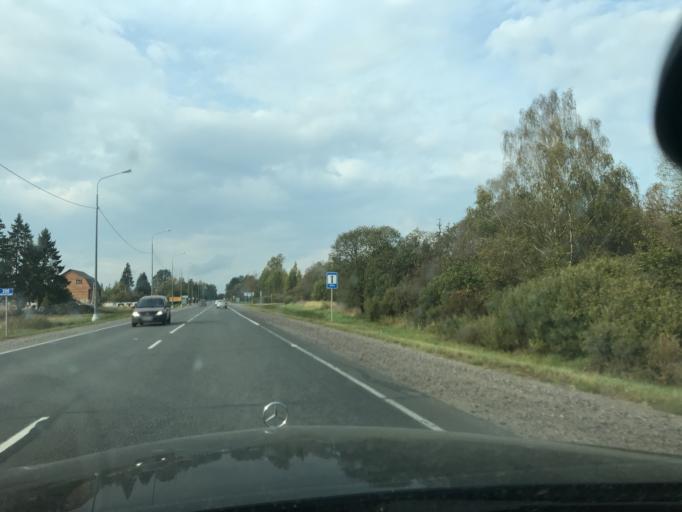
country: RU
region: Pskov
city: Ostrov
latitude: 57.2991
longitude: 28.3757
